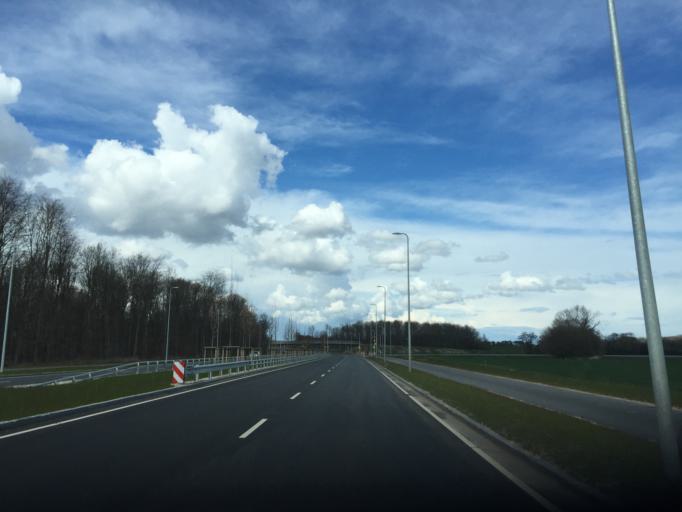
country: DK
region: South Denmark
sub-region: Odense Kommune
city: Hojby
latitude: 55.3601
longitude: 10.4144
